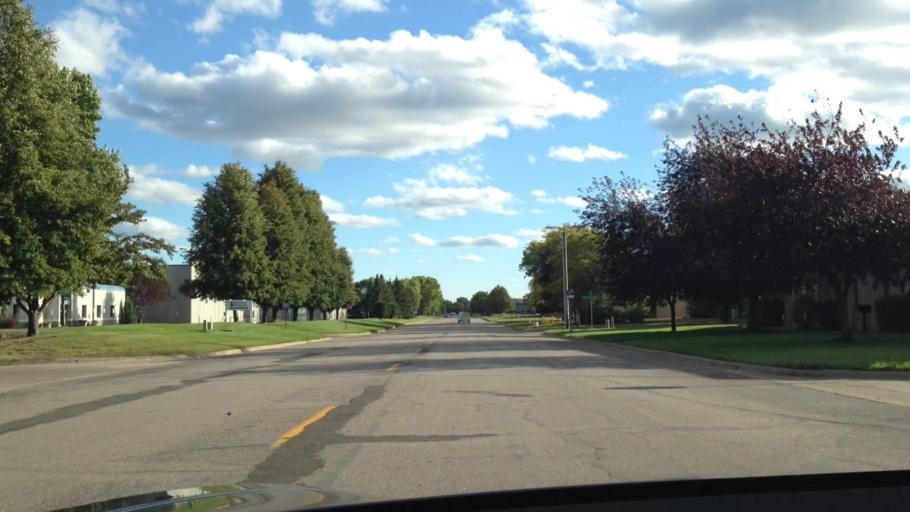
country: US
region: Minnesota
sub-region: Hennepin County
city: Osseo
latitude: 45.1150
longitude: -93.3869
